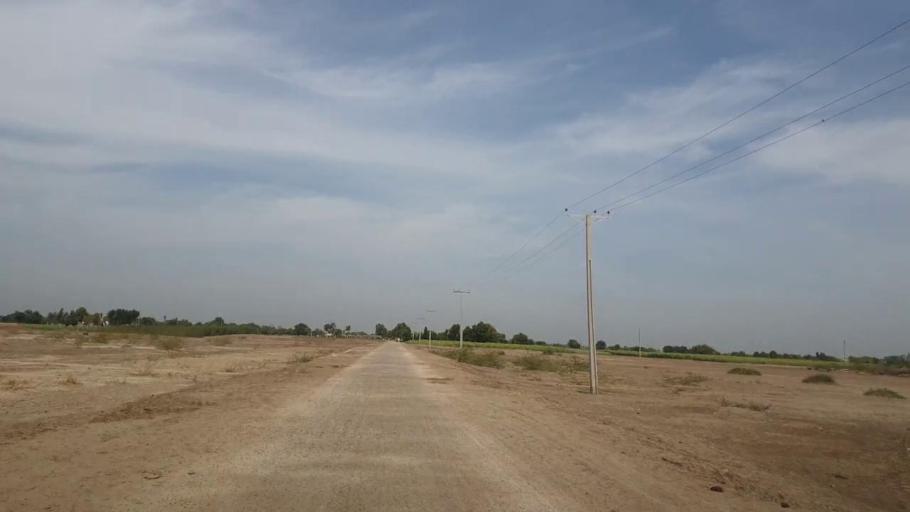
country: PK
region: Sindh
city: Kunri
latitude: 25.2132
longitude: 69.5838
